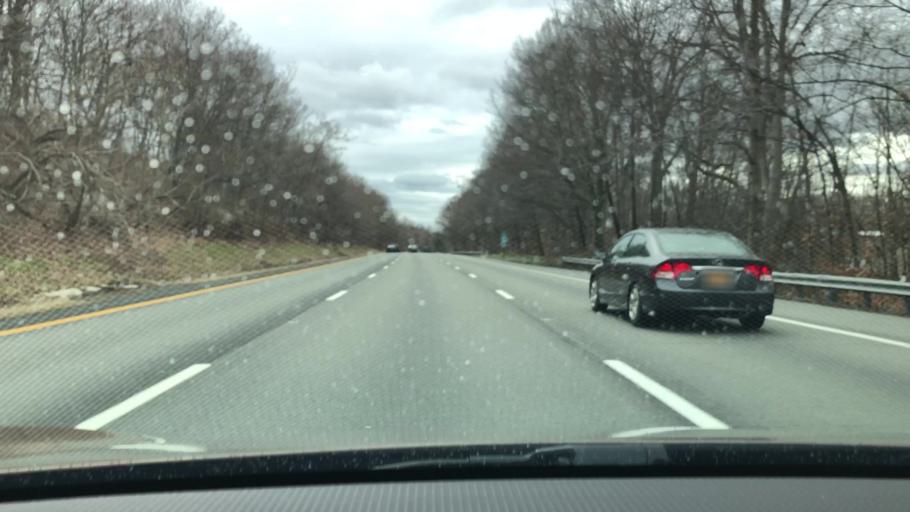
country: US
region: New Jersey
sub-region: Warren County
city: Belvidere
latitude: 40.9302
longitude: -75.0358
